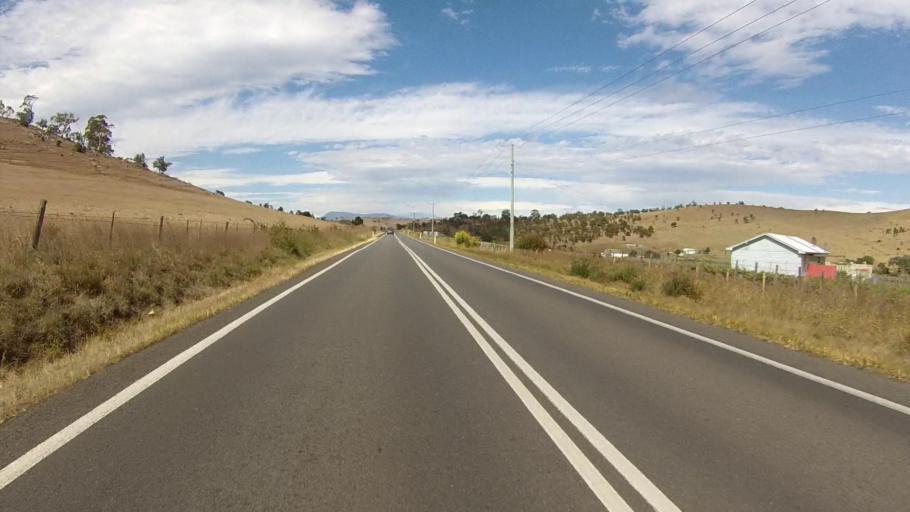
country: AU
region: Tasmania
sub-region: Brighton
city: Old Beach
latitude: -42.6780
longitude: 147.3561
